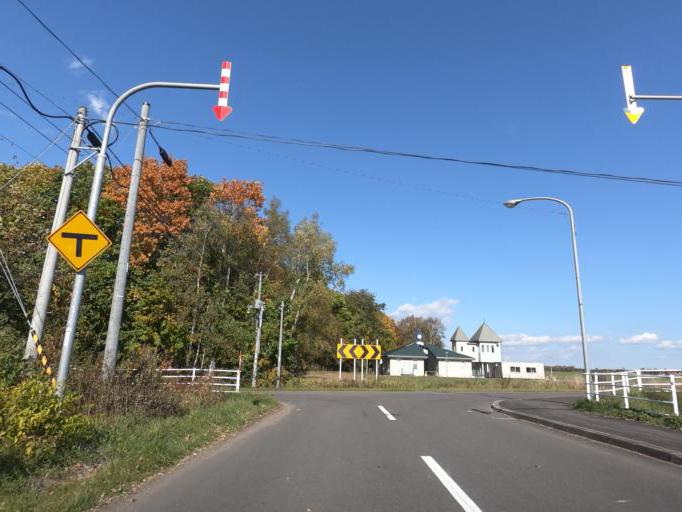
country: JP
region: Hokkaido
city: Otofuke
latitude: 43.2371
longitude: 143.2757
